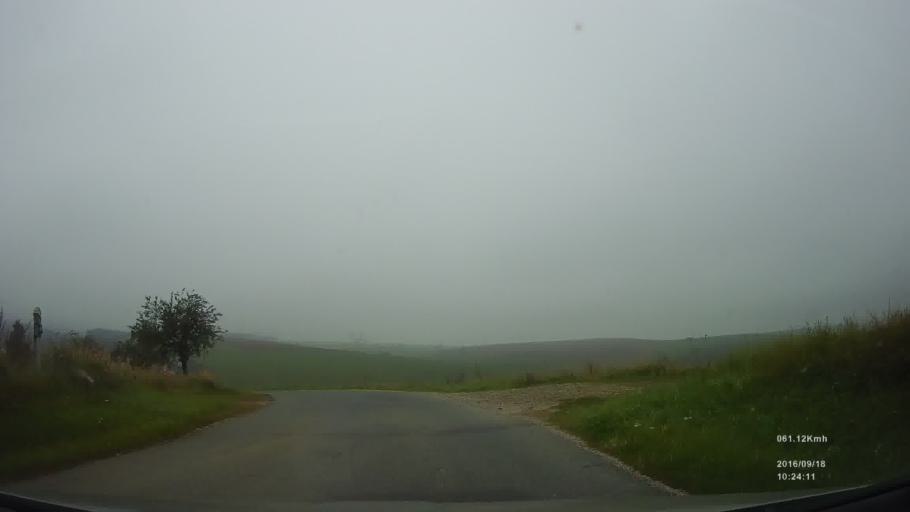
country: SK
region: Kosicky
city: Spisska Nova Ves
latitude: 48.9429
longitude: 20.6157
